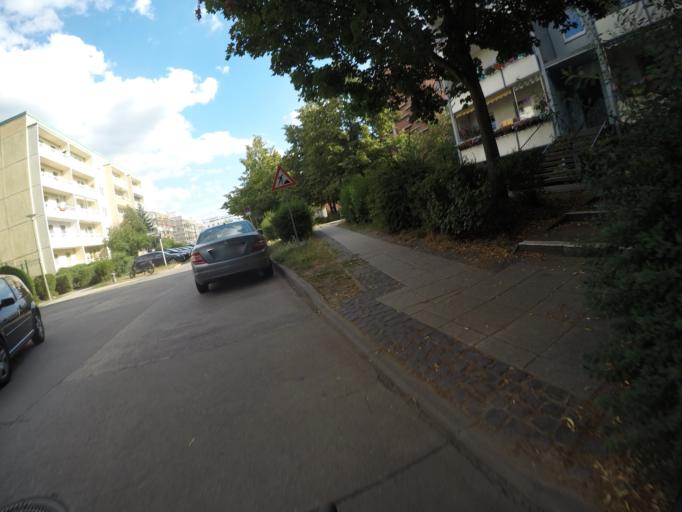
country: DE
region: Berlin
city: Hellersdorf
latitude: 52.5430
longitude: 13.6075
